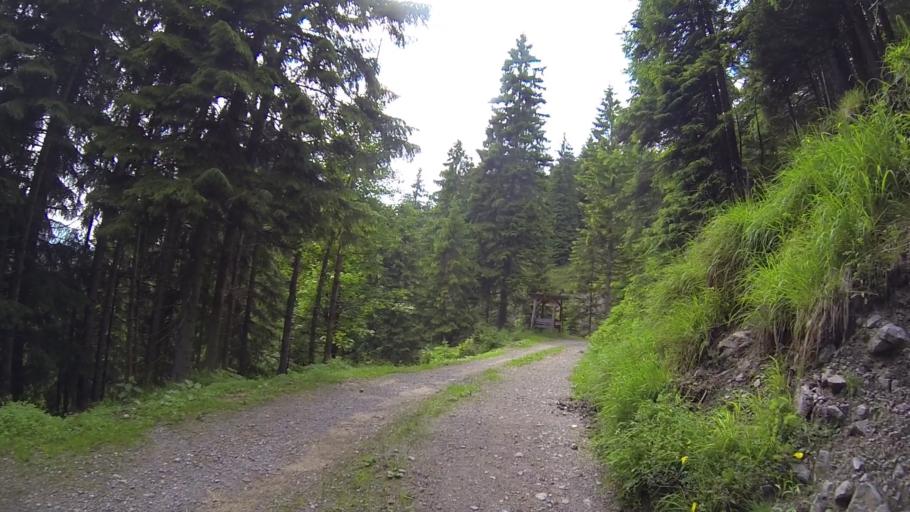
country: AT
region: Tyrol
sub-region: Politischer Bezirk Reutte
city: Breitenwang
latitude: 47.5029
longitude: 10.7773
